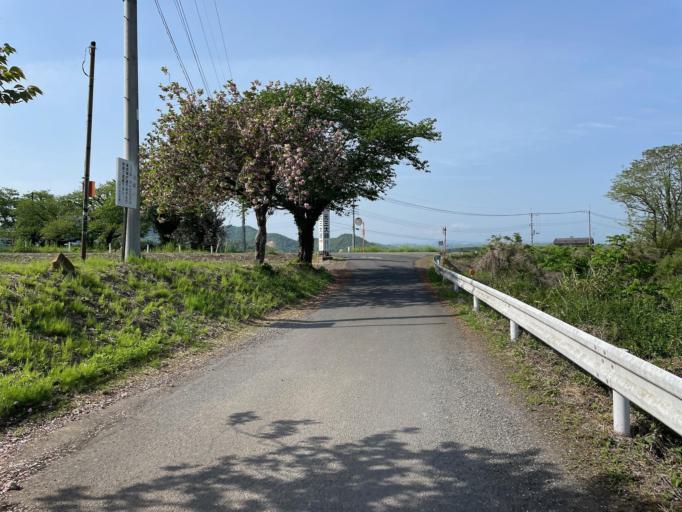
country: JP
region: Tochigi
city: Sano
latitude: 36.3102
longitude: 139.5362
